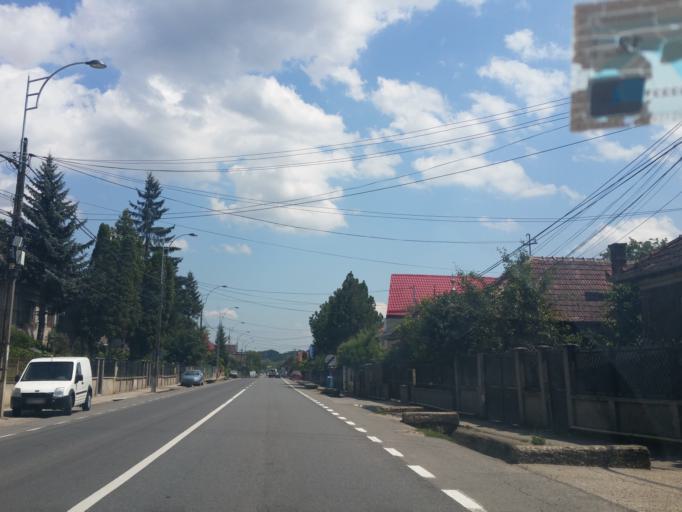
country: RO
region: Cluj
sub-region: Comuna Baciu
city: Baciu
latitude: 46.7870
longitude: 23.5316
